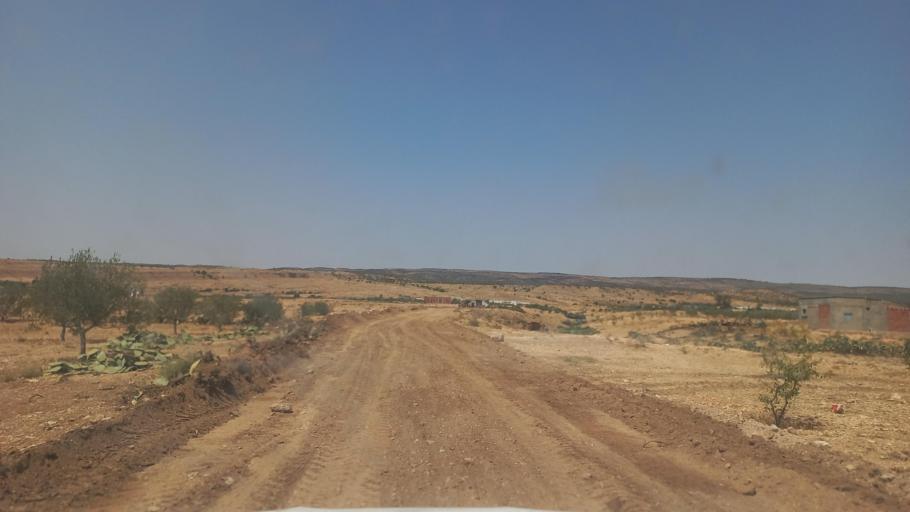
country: TN
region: Al Qasrayn
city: Kasserine
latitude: 35.2962
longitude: 8.9421
